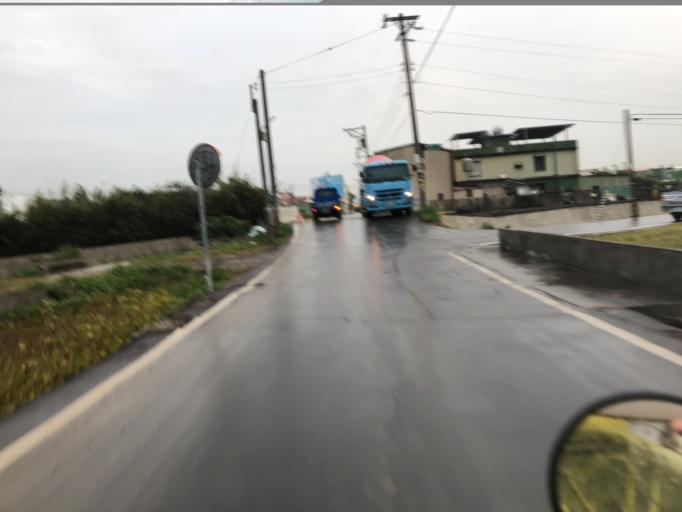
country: TW
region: Taiwan
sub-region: Hsinchu
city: Zhubei
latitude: 24.8432
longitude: 120.9863
